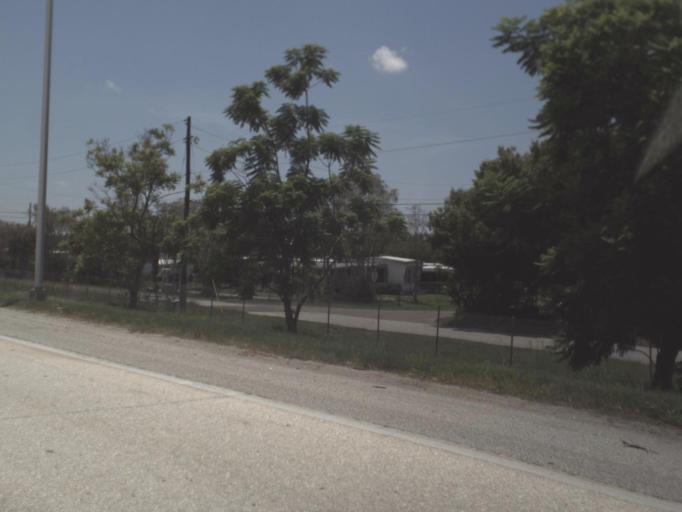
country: US
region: Florida
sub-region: Pinellas County
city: Lealman
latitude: 27.8143
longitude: -82.6649
